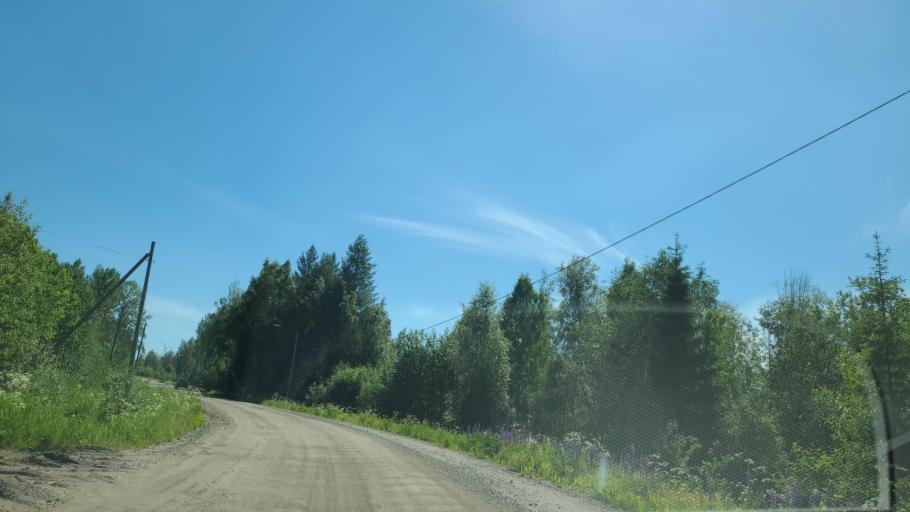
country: SE
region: Vaesterbotten
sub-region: Bjurholms Kommun
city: Bjurholm
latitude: 63.6911
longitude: 18.9569
